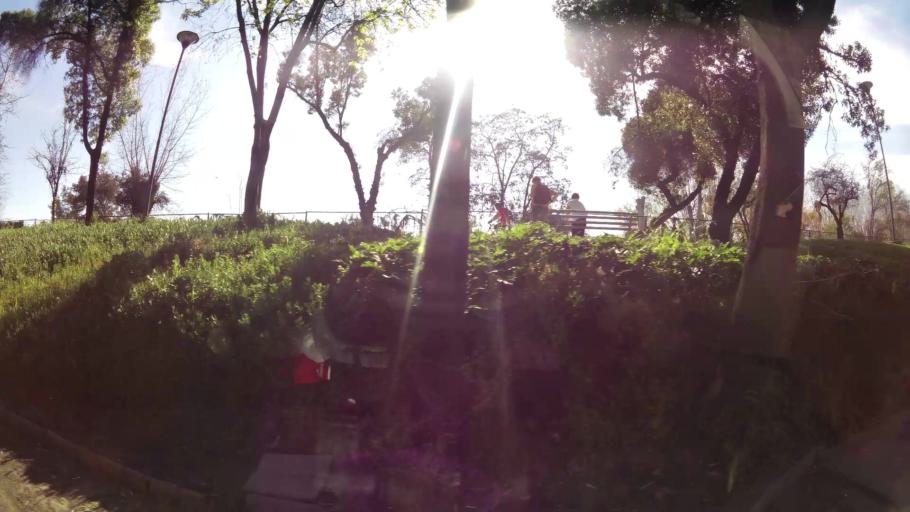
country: CL
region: Santiago Metropolitan
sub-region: Provincia de Santiago
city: Villa Presidente Frei, Nunoa, Santiago, Chile
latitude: -33.4419
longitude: -70.5698
